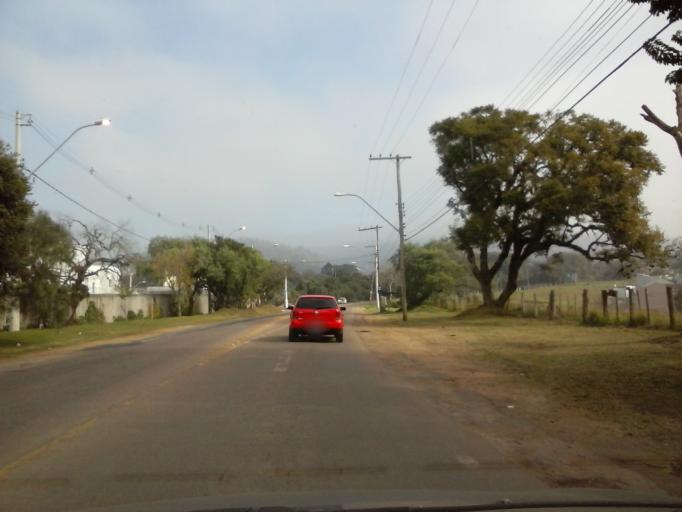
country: BR
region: Rio Grande do Sul
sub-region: Viamao
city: Viamao
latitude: -30.0475
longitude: -51.0928
